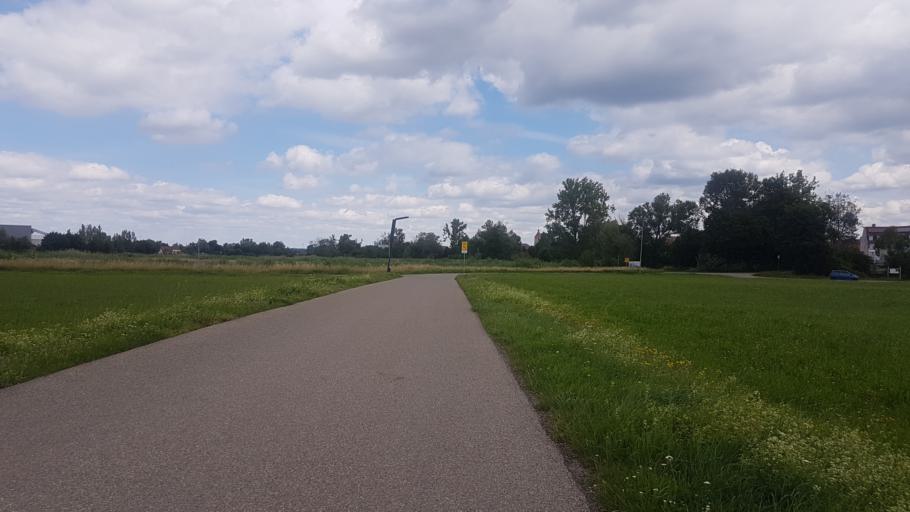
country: DE
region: Bavaria
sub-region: Regierungsbezirk Mittelfranken
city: Gunzenhausen
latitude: 49.1085
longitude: 10.7524
